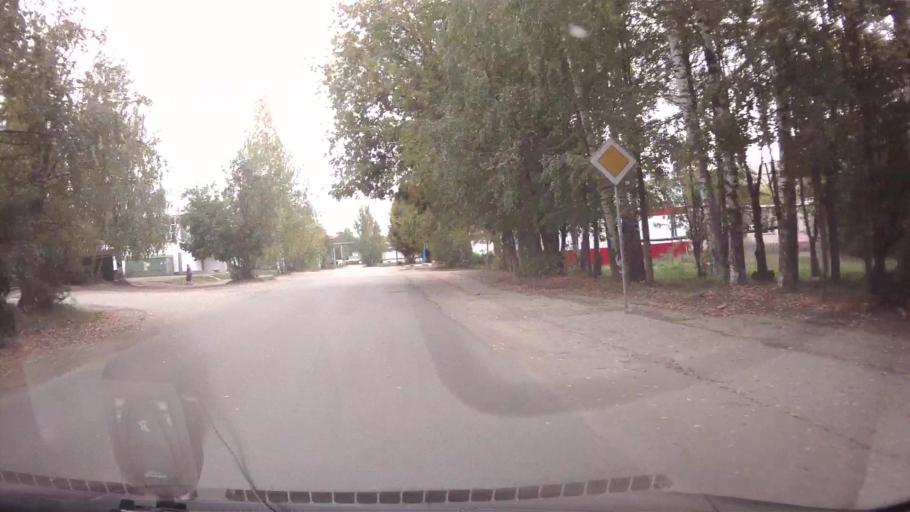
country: RU
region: Mariy-El
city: Kuzhener
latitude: 57.0022
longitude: 48.7406
